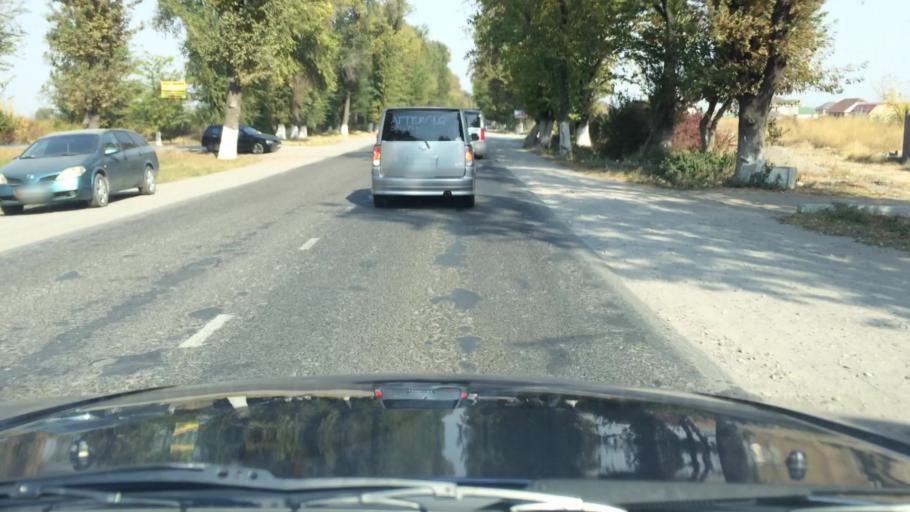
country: KG
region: Chuy
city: Lebedinovka
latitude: 42.9147
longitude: 74.6885
